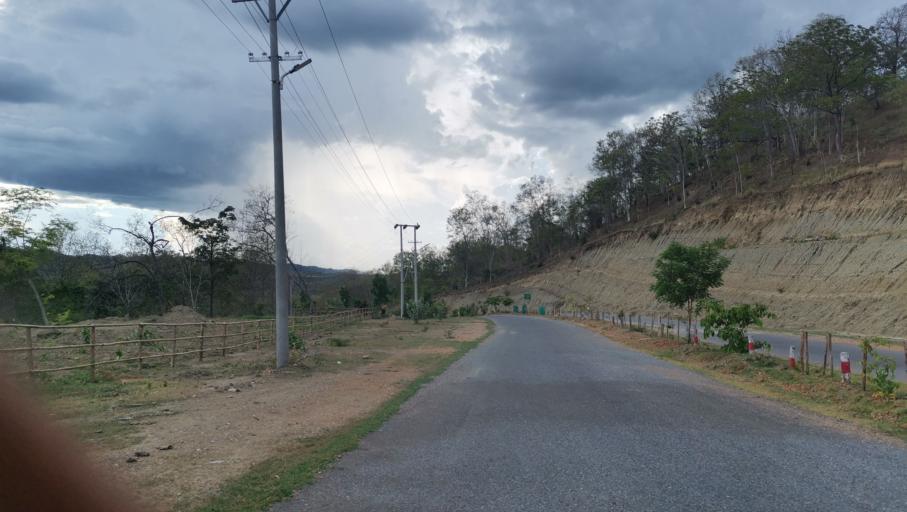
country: MM
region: Magway
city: Minbu
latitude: 20.1053
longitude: 94.5448
